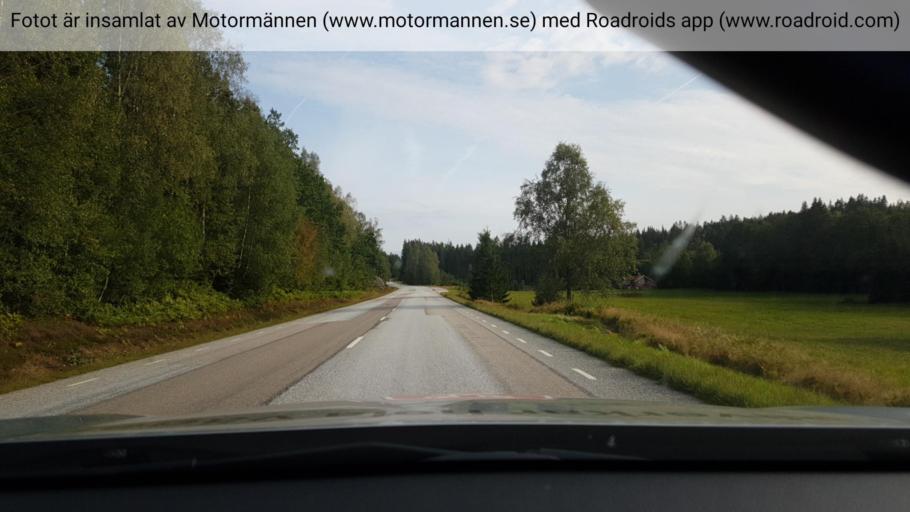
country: SE
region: Vaestra Goetaland
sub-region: Uddevalla Kommun
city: Ljungskile
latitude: 58.1780
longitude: 11.9614
